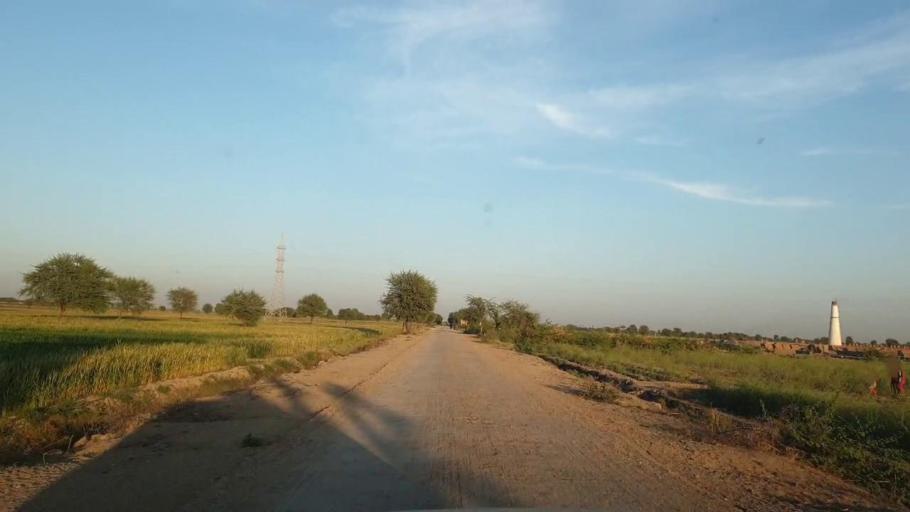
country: PK
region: Sindh
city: Kunri
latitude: 25.1289
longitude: 69.4357
